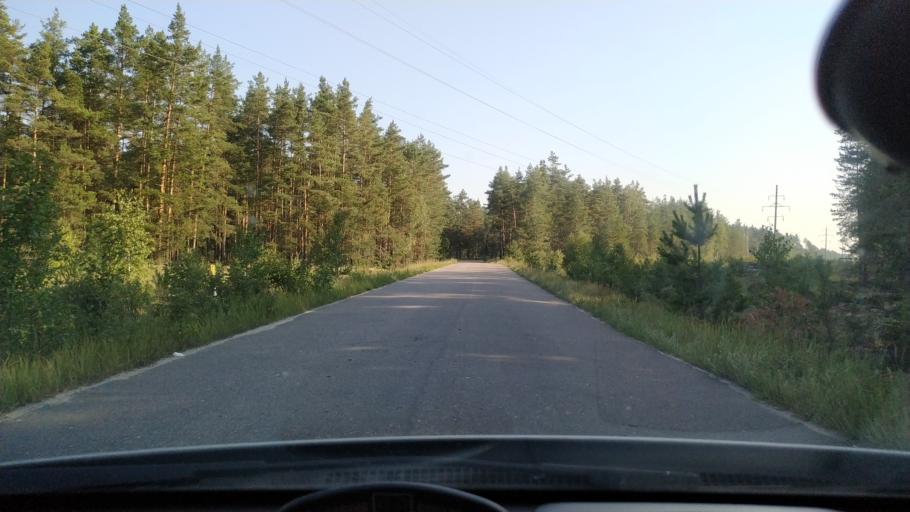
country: RU
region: Moskovskaya
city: Roshal'
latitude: 55.6551
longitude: 39.8003
